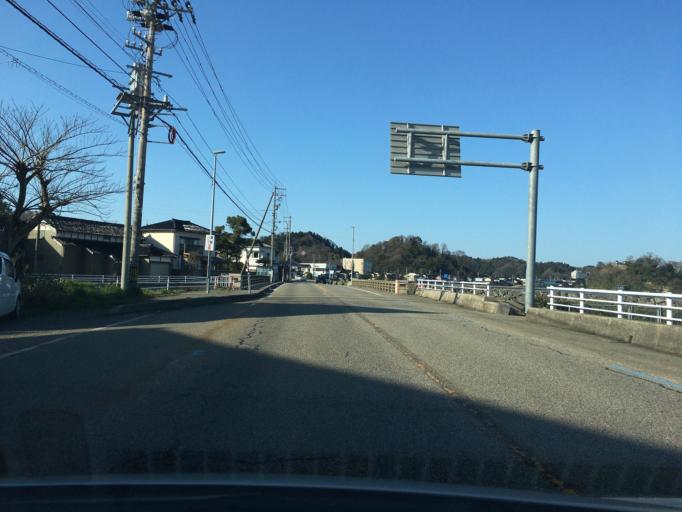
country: JP
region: Toyama
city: Himi
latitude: 36.8748
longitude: 136.9843
